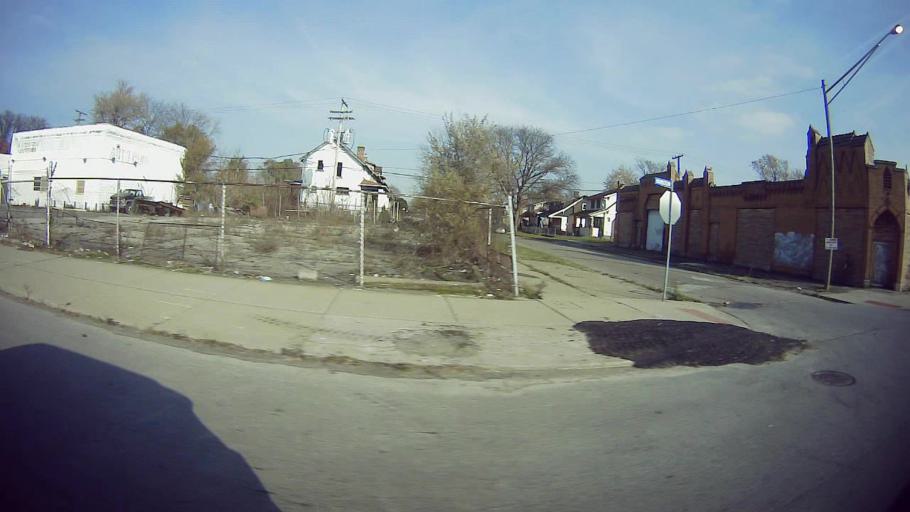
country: US
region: Michigan
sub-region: Wayne County
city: Highland Park
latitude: 42.4161
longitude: -83.1153
